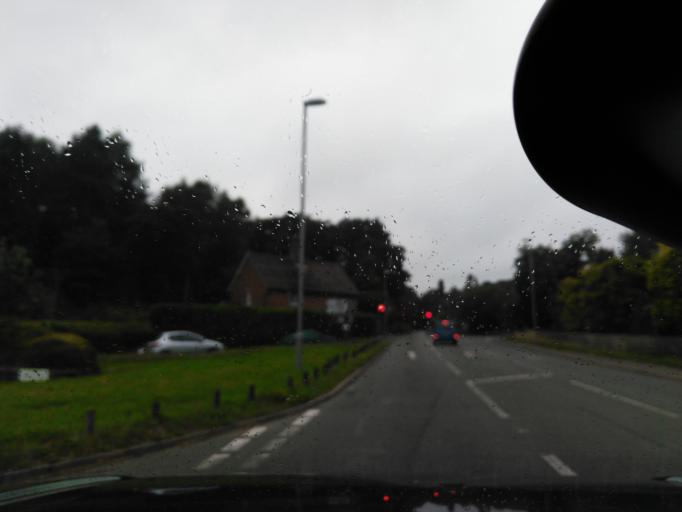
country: GB
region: England
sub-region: Dorset
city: Lytchett Matravers
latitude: 50.7512
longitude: -2.0433
